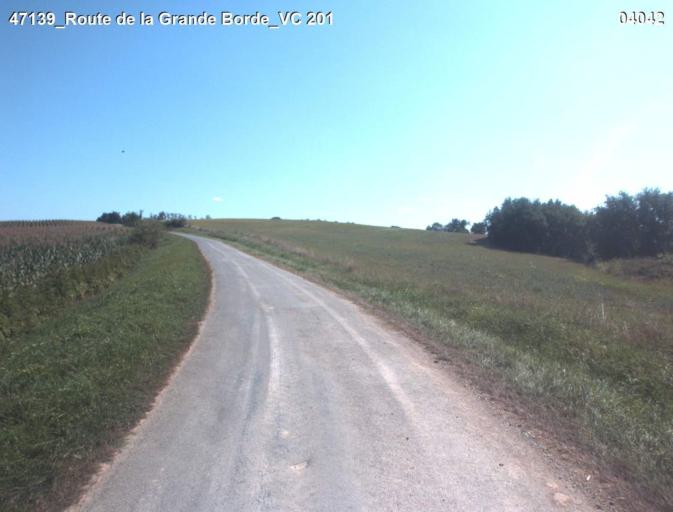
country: FR
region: Aquitaine
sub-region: Departement du Lot-et-Garonne
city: Nerac
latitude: 44.0935
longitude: 0.3750
